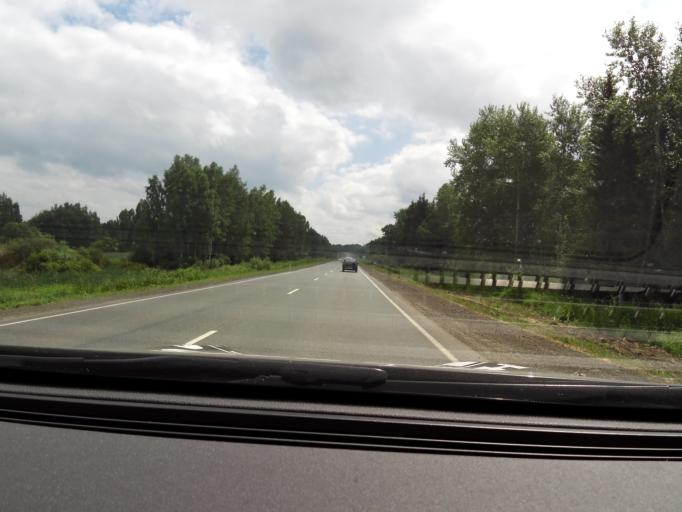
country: RU
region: Perm
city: Kungur
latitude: 57.4640
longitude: 56.7568
